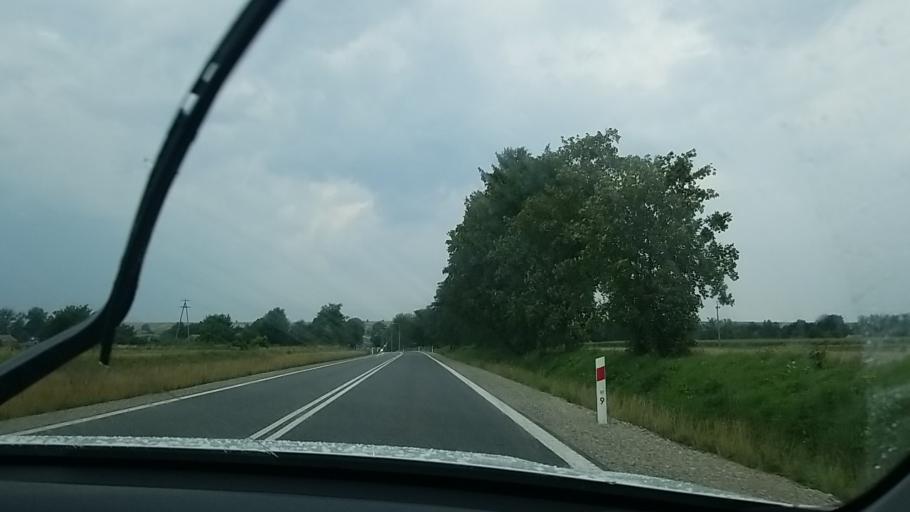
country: PL
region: Lublin Voivodeship
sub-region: Powiat lubelski
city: Wysokie
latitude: 50.9526
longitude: 22.6779
